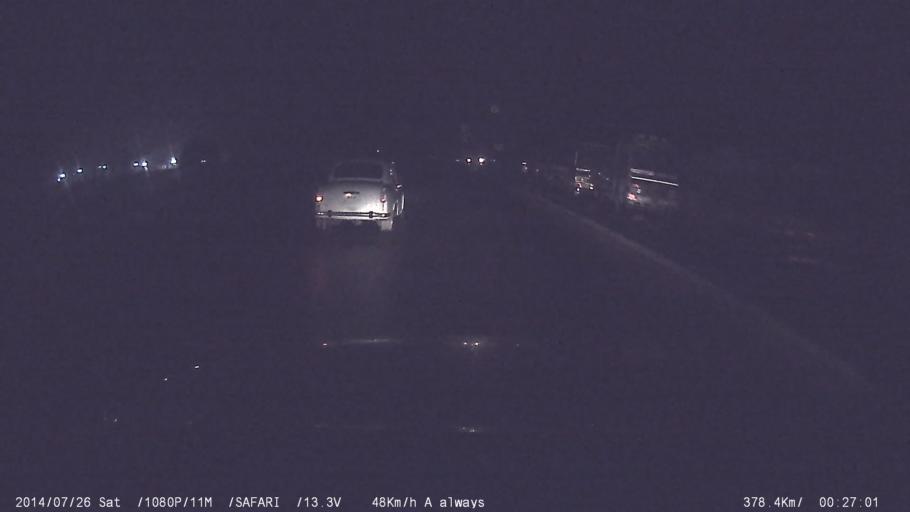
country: IN
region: Tamil Nadu
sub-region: Coimbatore
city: Madukkarai
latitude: 10.8312
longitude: 76.8309
